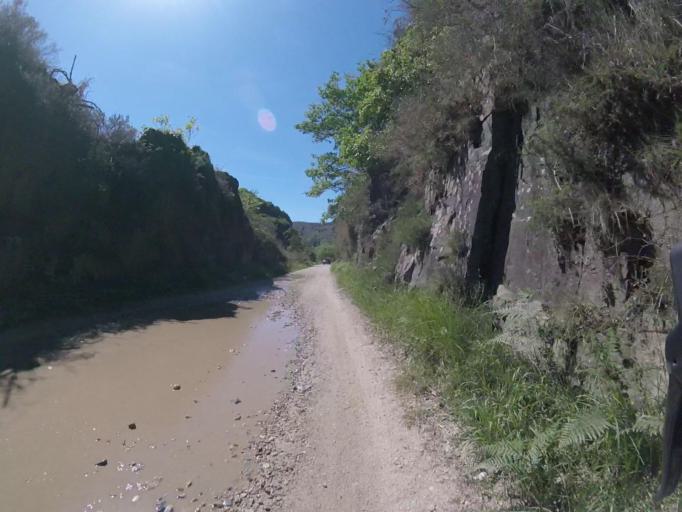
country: ES
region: Navarre
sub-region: Provincia de Navarra
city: Bera
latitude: 43.2865
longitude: -1.7129
